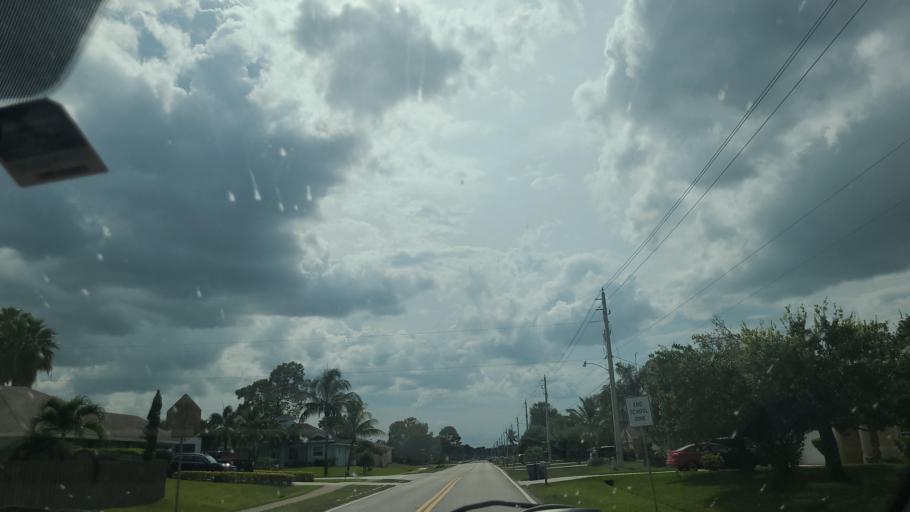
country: US
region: Florida
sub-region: Saint Lucie County
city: Port Saint Lucie
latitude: 27.2425
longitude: -80.3662
